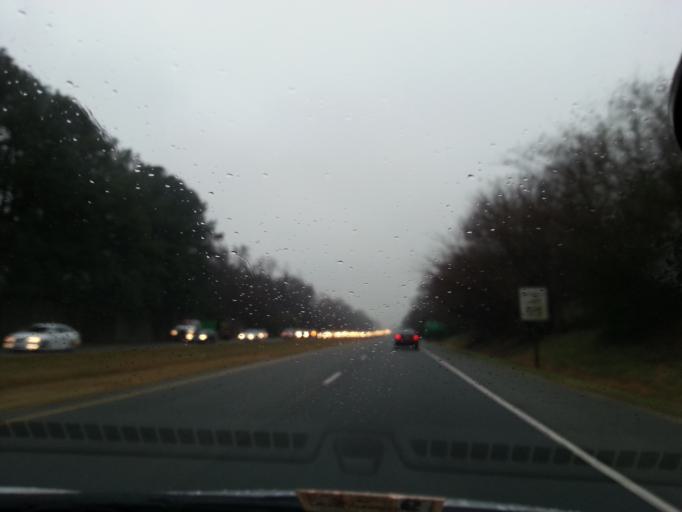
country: US
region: Virginia
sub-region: City of Chesapeake
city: Chesapeake
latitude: 36.7011
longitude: -76.2269
